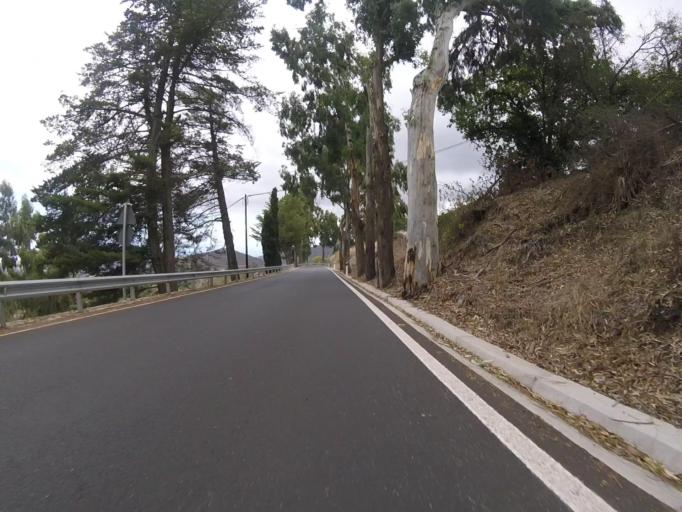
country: ES
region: Canary Islands
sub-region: Provincia de Las Palmas
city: Vega de San Mateo
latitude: 28.0080
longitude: -15.5550
